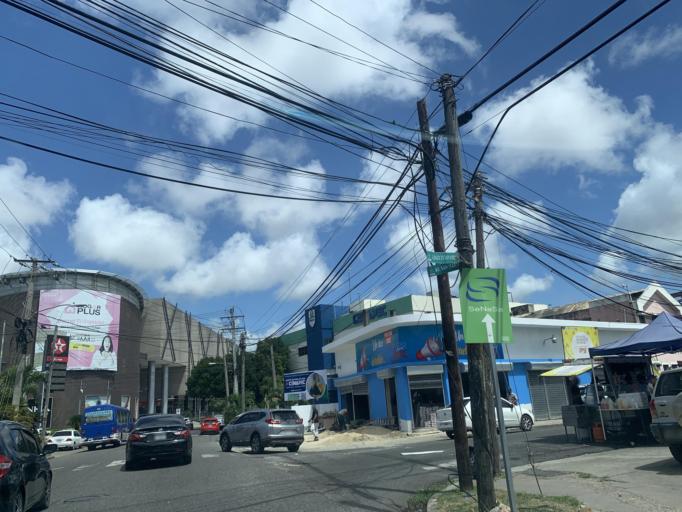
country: DO
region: Nacional
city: San Carlos
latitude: 18.4827
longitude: -69.9098
